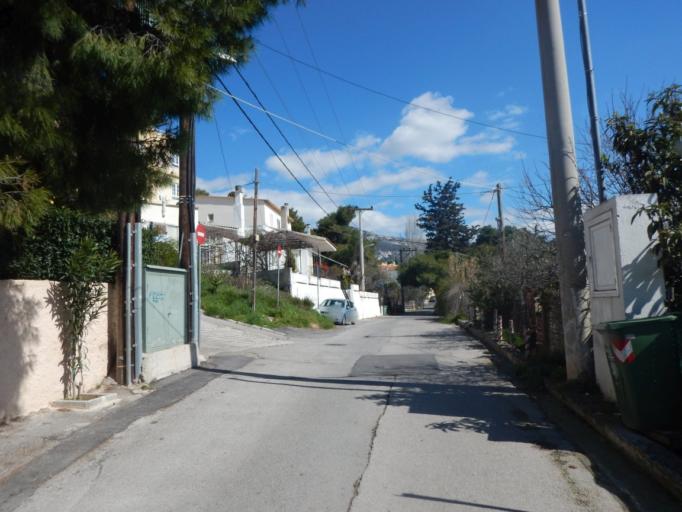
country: GR
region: Attica
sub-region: Nomarchia Athinas
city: Melissia
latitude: 38.0648
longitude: 23.8333
